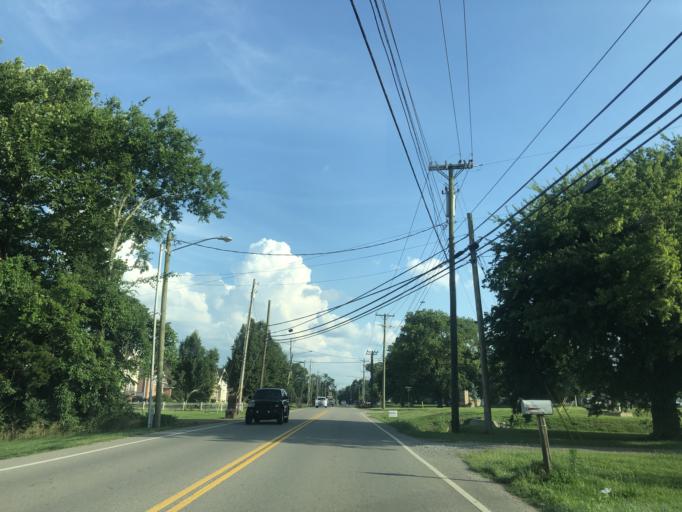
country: US
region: Tennessee
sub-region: Davidson County
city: Nashville
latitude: 36.2559
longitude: -86.8302
